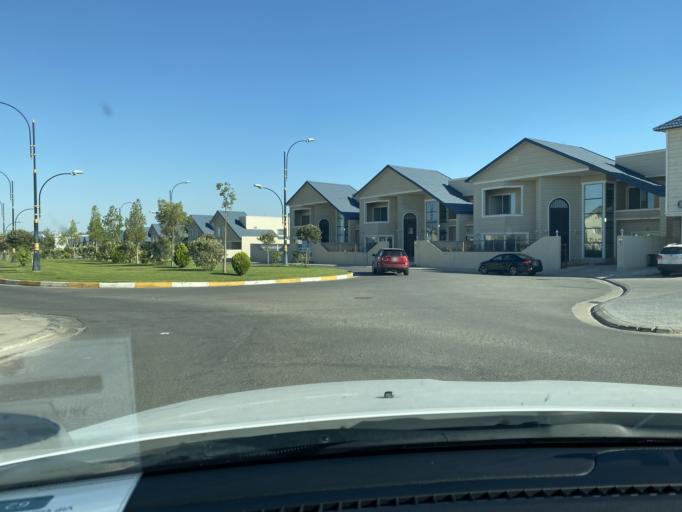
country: IQ
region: Arbil
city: Erbil
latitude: 36.2436
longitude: 44.0477
